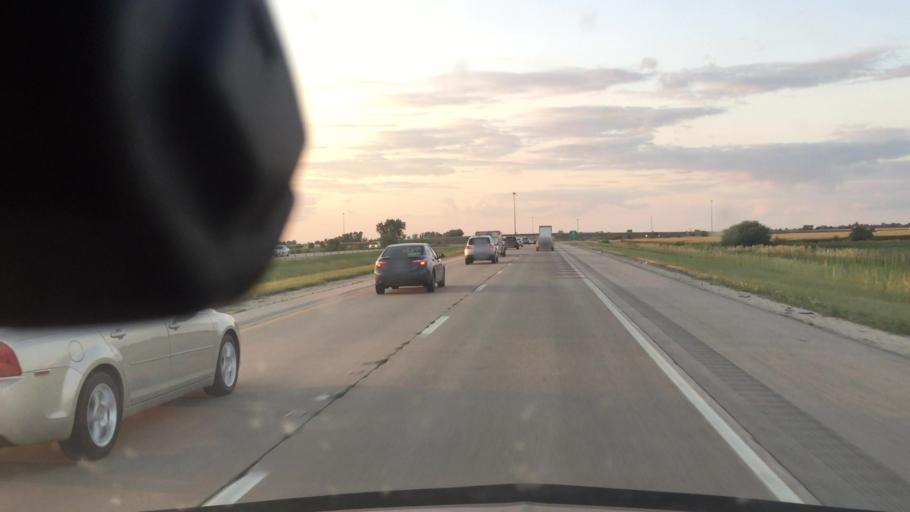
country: US
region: Illinois
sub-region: Livingston County
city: Dwight
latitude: 41.0847
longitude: -88.4517
